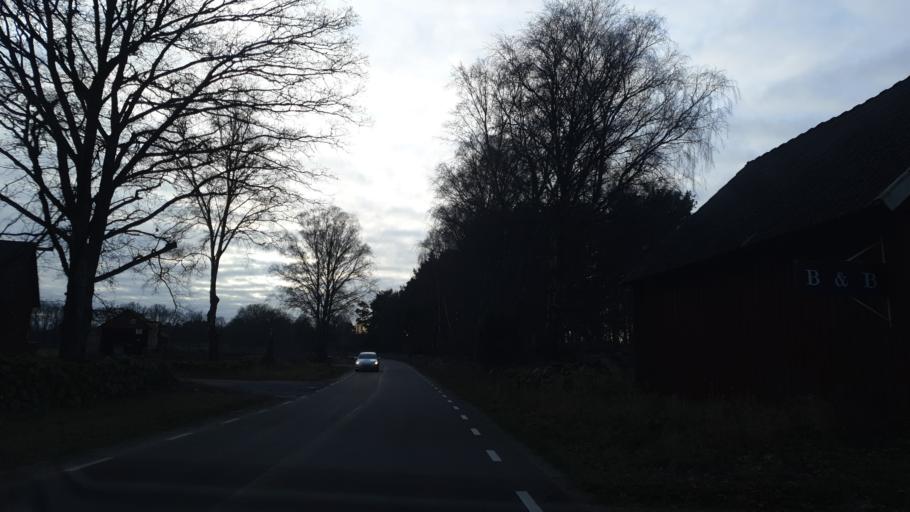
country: SE
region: Kalmar
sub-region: Torsas Kommun
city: Torsas
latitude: 56.2307
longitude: 15.9958
